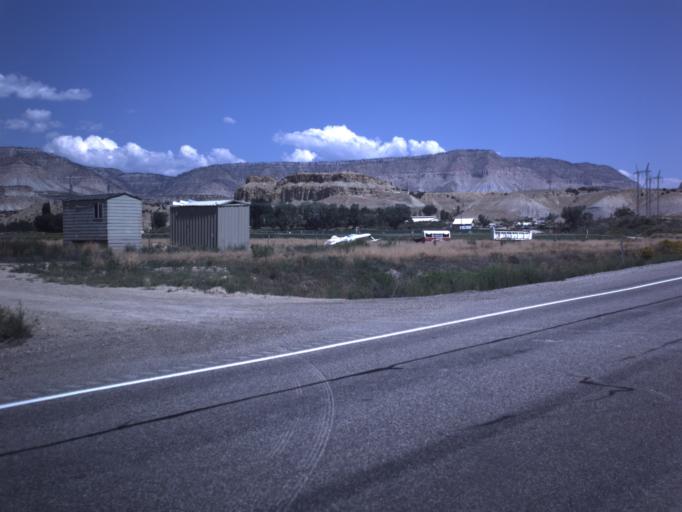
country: US
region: Utah
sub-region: Emery County
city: Ferron
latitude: 38.8771
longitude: -111.2903
